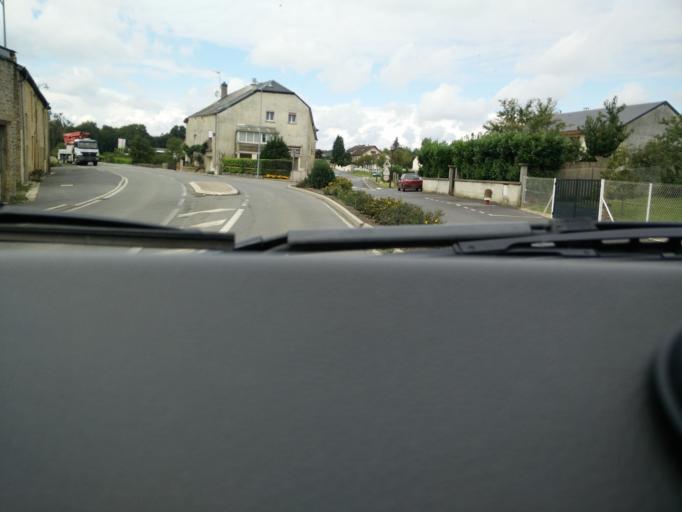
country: FR
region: Champagne-Ardenne
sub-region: Departement des Ardennes
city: Renwez
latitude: 49.8118
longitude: 4.6114
